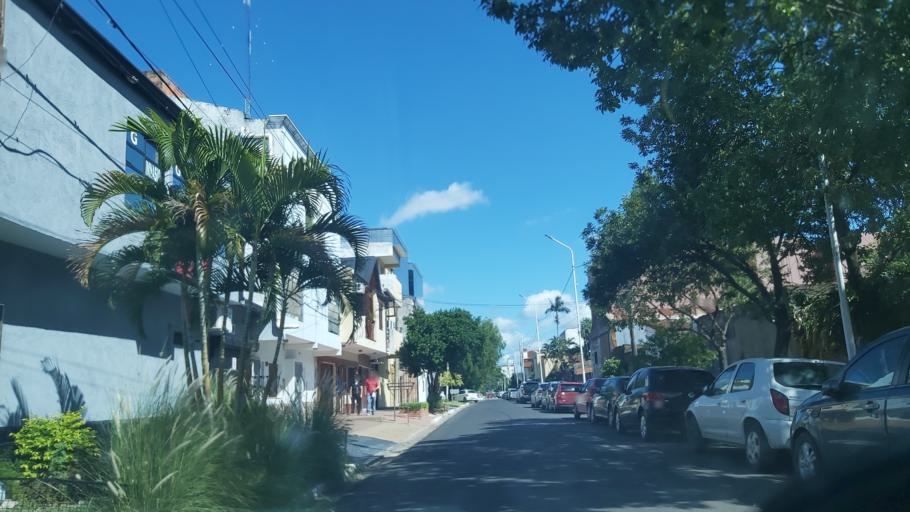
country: AR
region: Corrientes
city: Corrientes
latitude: -27.4754
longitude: -58.8444
